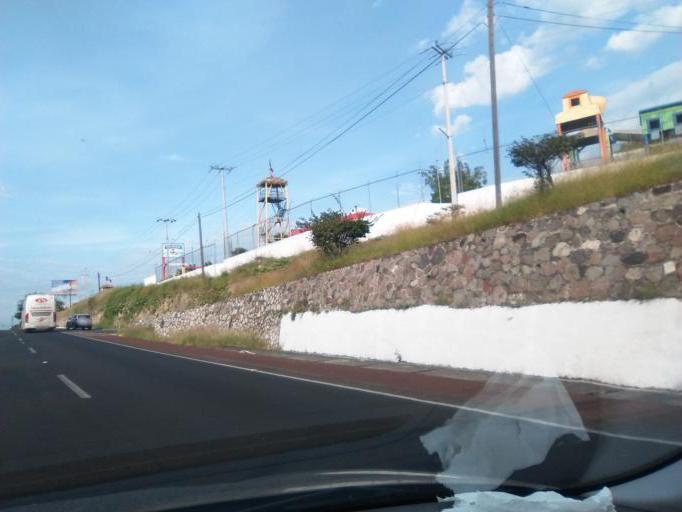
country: MX
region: Morelos
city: Alpuyeca
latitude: 18.7411
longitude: -99.2490
